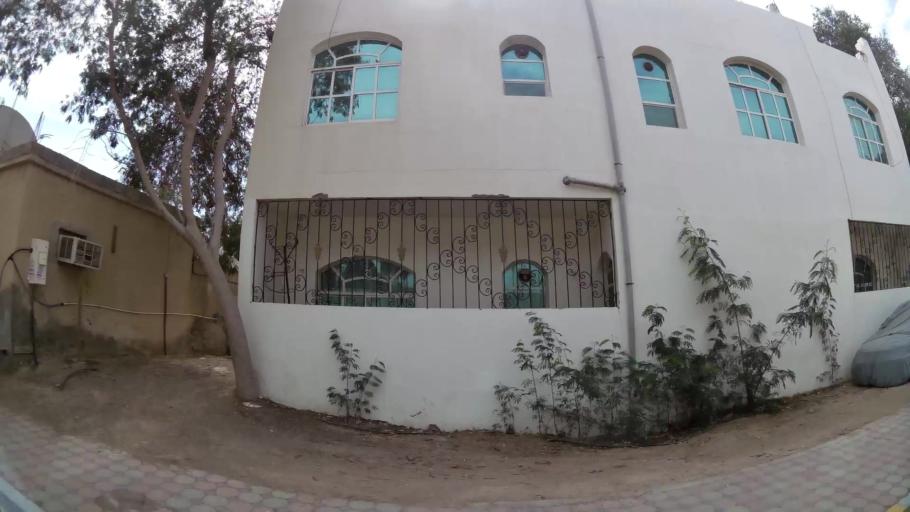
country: OM
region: Al Buraimi
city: Al Buraymi
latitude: 24.2237
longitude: 55.7776
